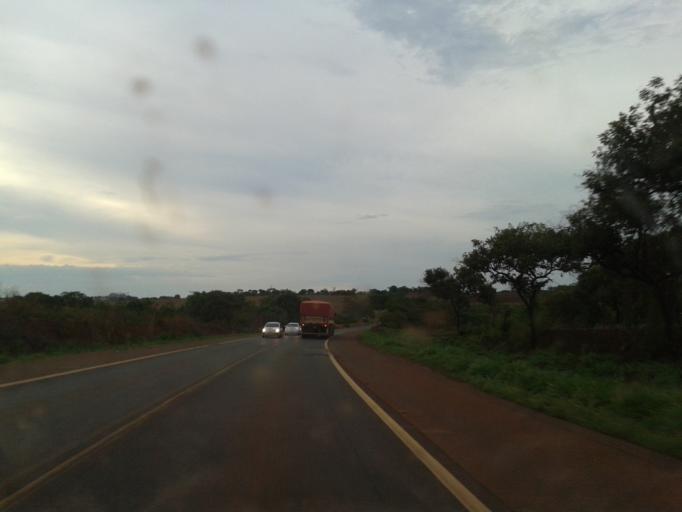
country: BR
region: Goias
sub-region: Santa Helena De Goias
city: Santa Helena de Goias
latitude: -17.9537
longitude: -50.5089
